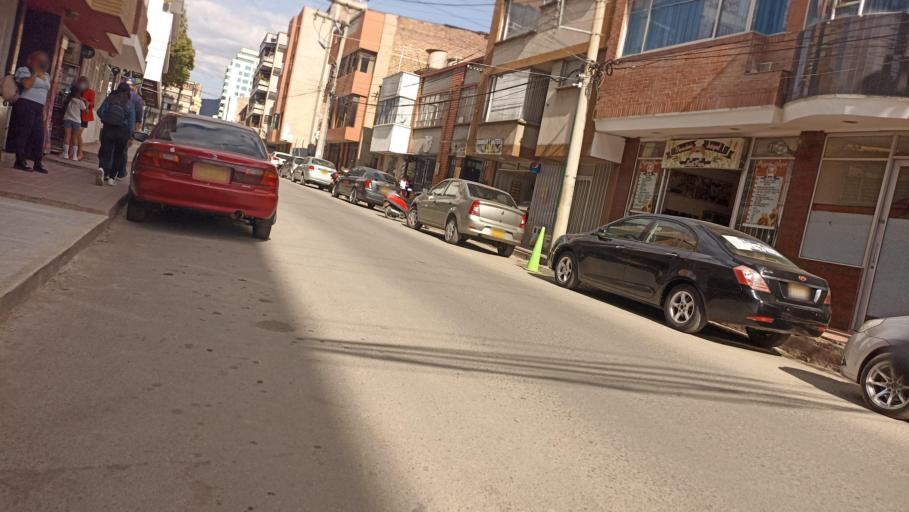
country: CO
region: Boyaca
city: Duitama
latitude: 5.8264
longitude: -73.0371
